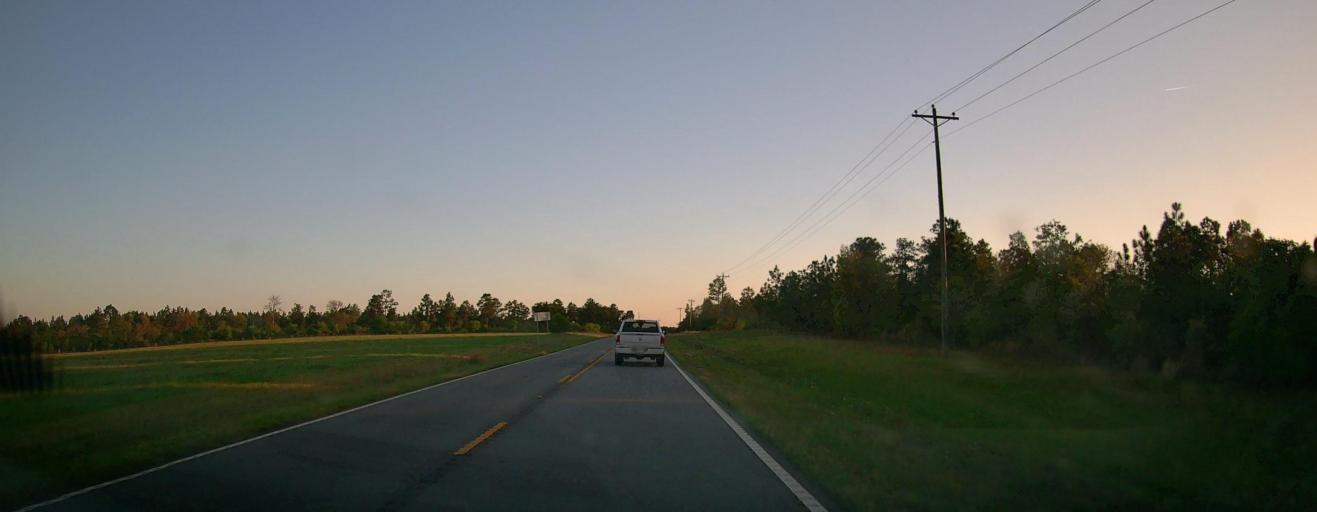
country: US
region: Georgia
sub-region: Talbot County
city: Talbotton
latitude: 32.4961
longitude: -84.6142
